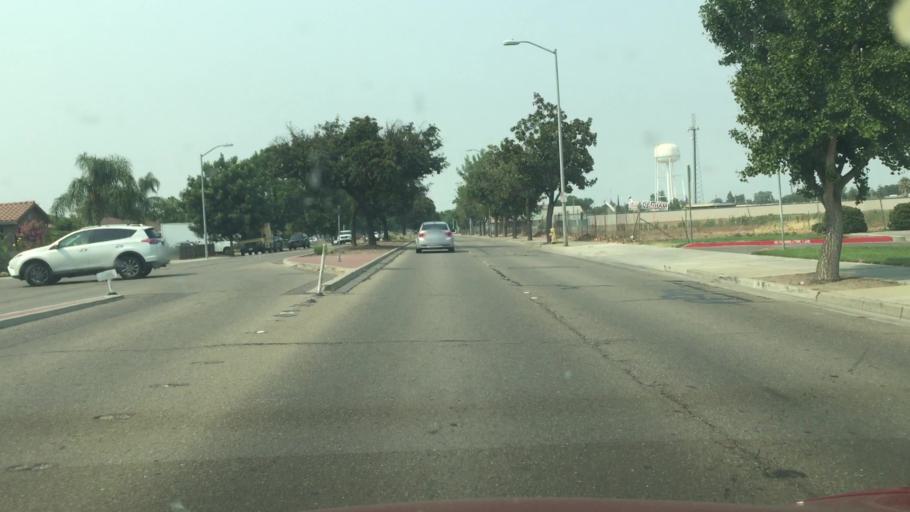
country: US
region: California
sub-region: San Joaquin County
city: Manteca
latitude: 37.7891
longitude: -121.2160
